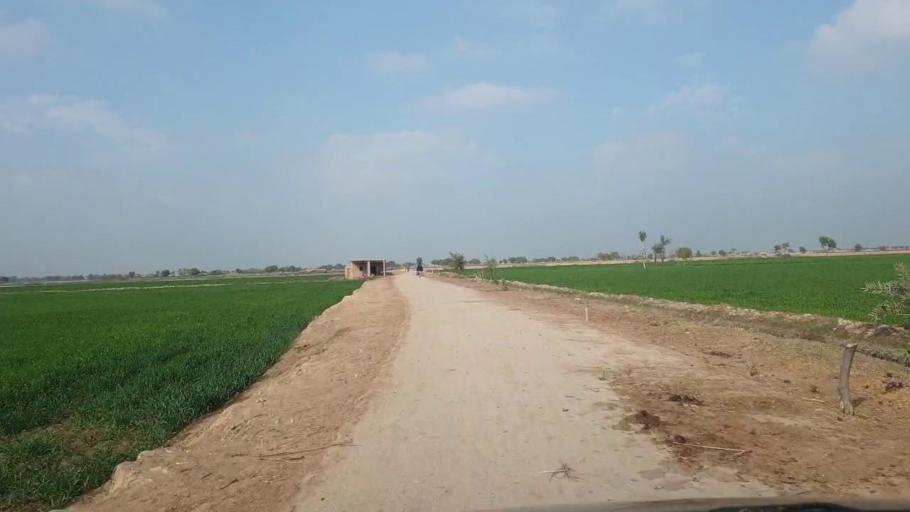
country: PK
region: Sindh
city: Shahdadpur
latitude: 25.9049
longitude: 68.6616
